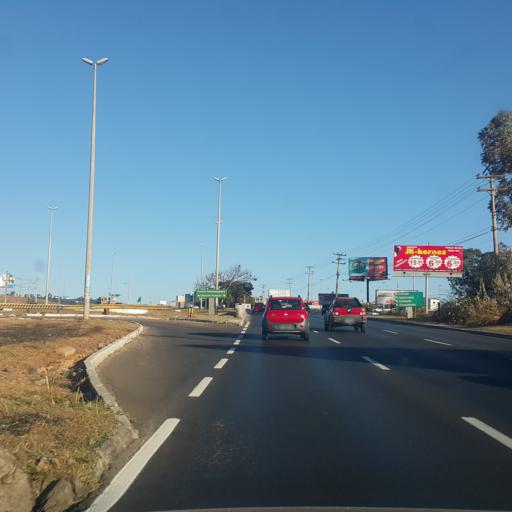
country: BR
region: Federal District
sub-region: Brasilia
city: Brasilia
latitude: -15.8352
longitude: -48.0710
